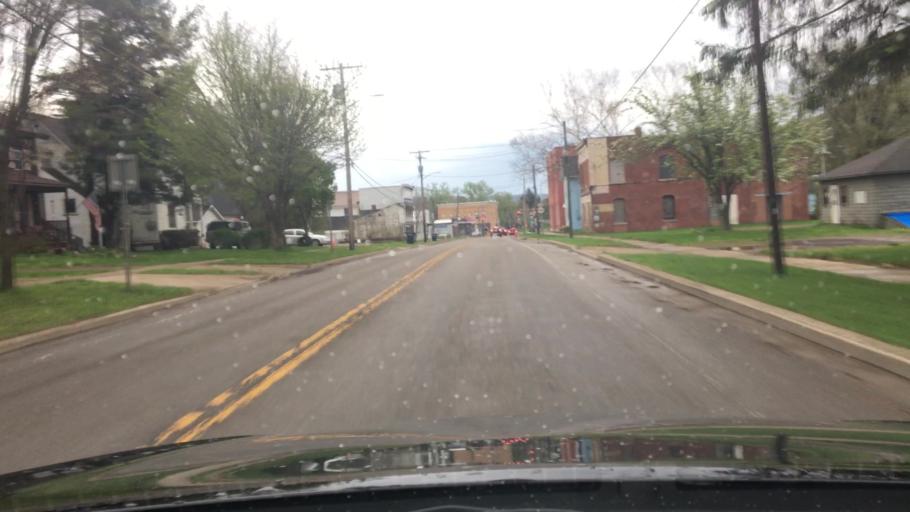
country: US
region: New York
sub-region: Cattaraugus County
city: Little Valley
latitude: 42.2506
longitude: -78.8011
